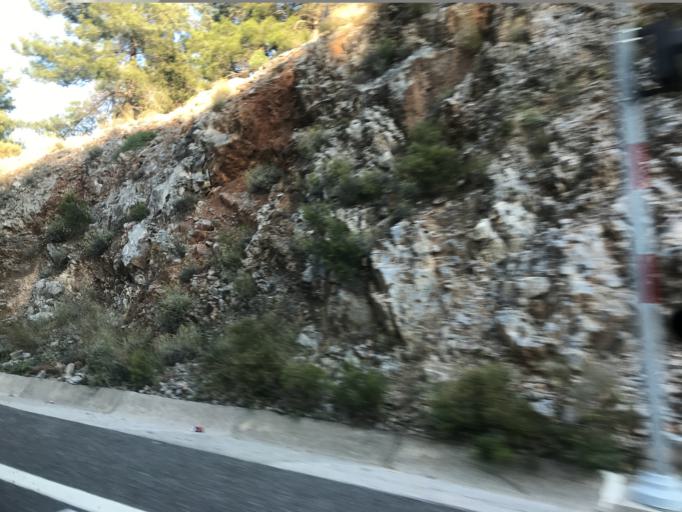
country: TR
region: Mugla
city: Ula
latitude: 37.0599
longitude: 28.3554
